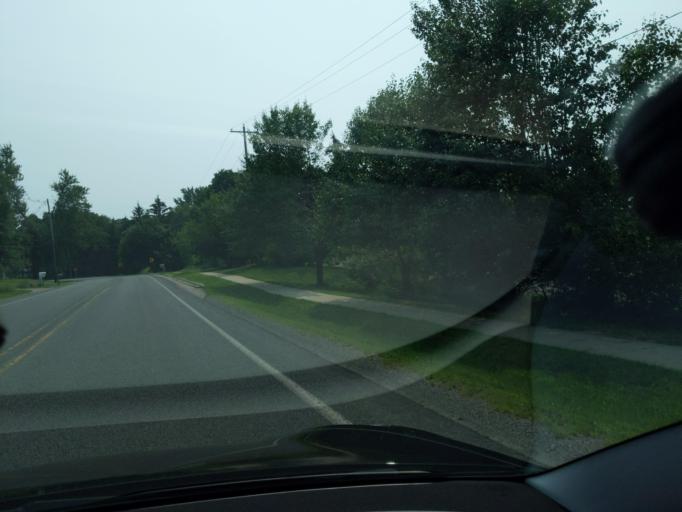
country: US
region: Michigan
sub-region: Ingham County
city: Holt
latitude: 42.6513
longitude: -84.5670
